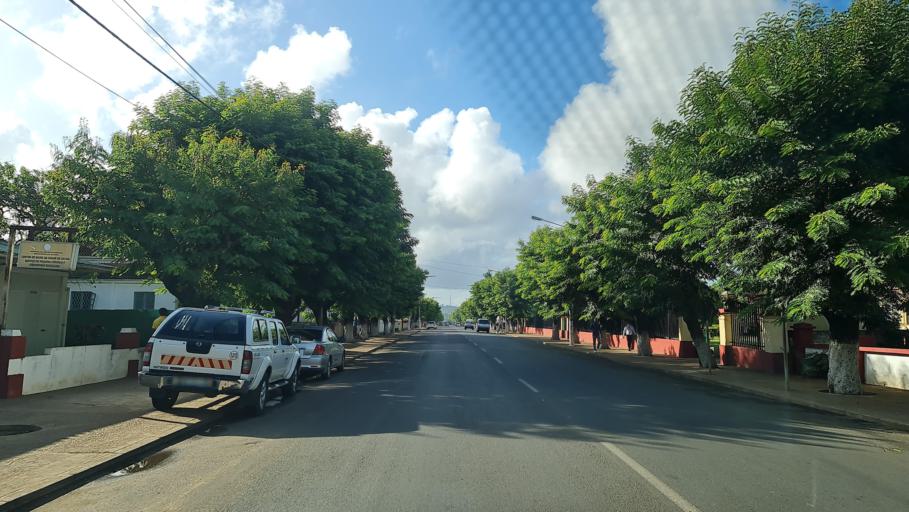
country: MZ
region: Gaza
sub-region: Xai-Xai District
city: Xai-Xai
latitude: -25.0375
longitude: 33.6382
